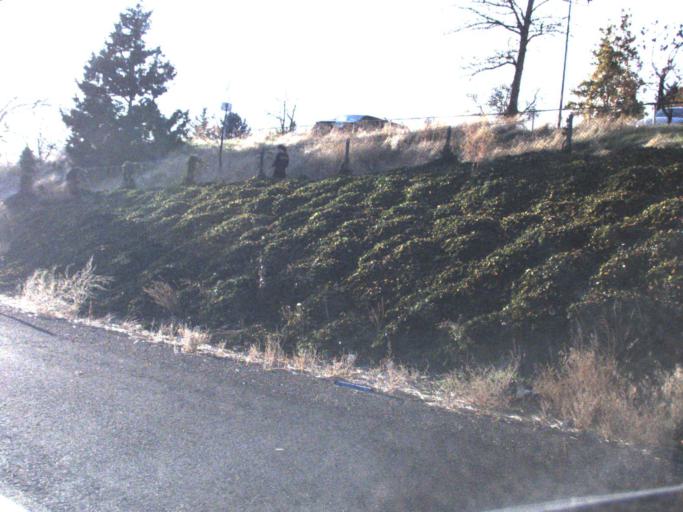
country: US
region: Washington
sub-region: Walla Walla County
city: Walla Walla
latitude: 46.0773
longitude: -118.3375
